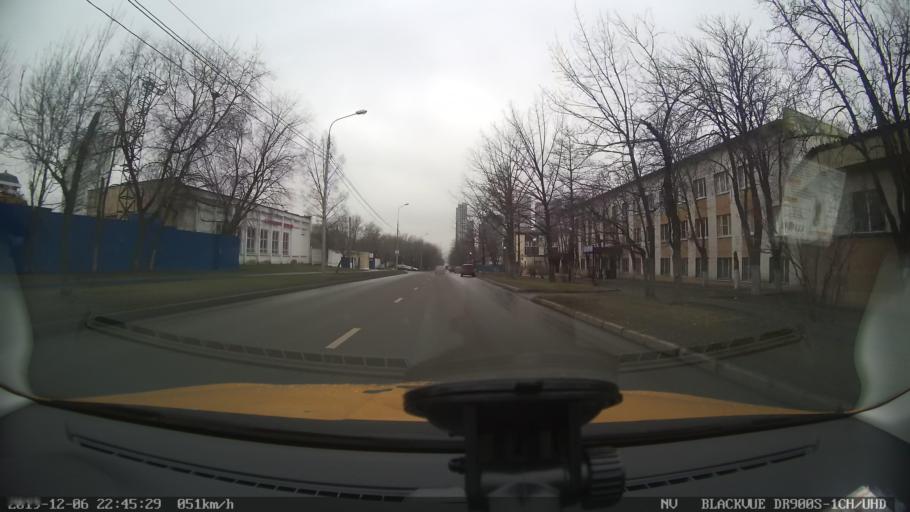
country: RU
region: Moscow
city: Metrogorodok
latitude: 55.8108
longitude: 37.7718
